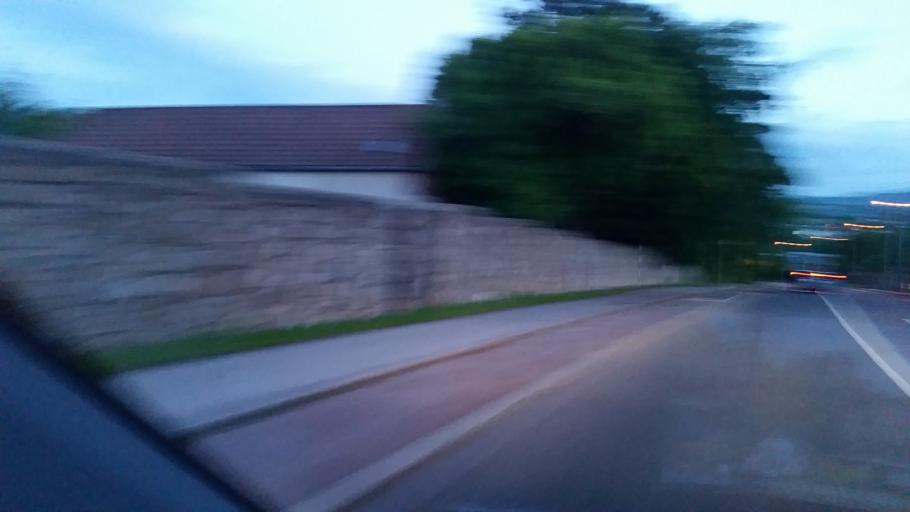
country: IE
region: Leinster
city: Foxrock
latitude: 53.2575
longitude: -6.1705
